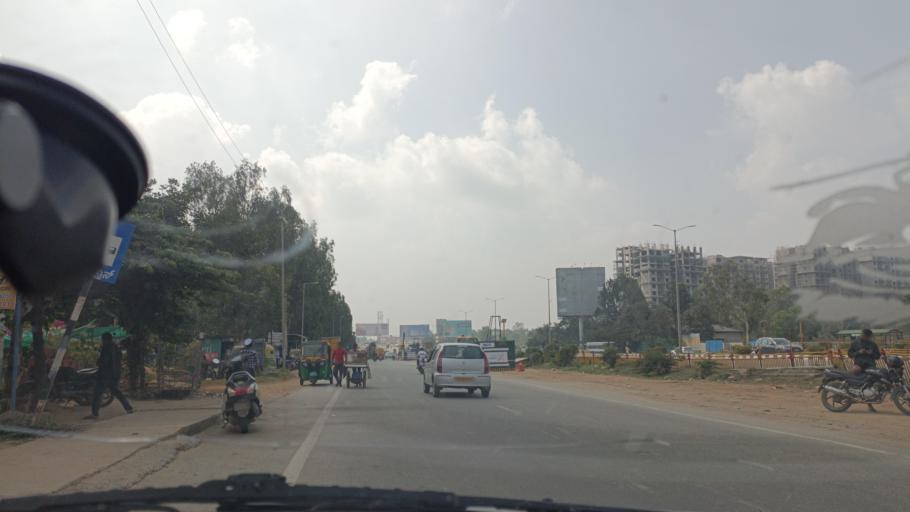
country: IN
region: Karnataka
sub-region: Bangalore Urban
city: Yelahanka
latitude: 13.1519
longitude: 77.6206
